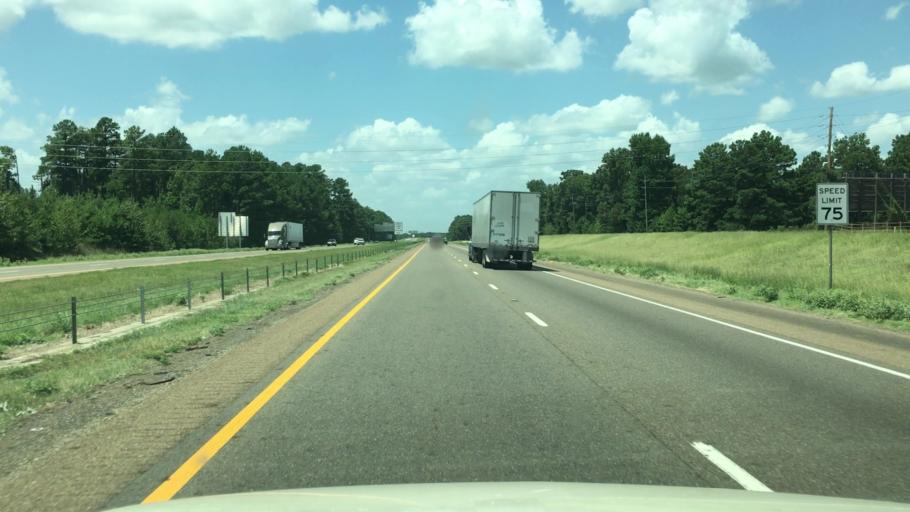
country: US
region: Texas
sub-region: Bowie County
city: Nash
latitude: 33.4555
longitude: -94.1423
